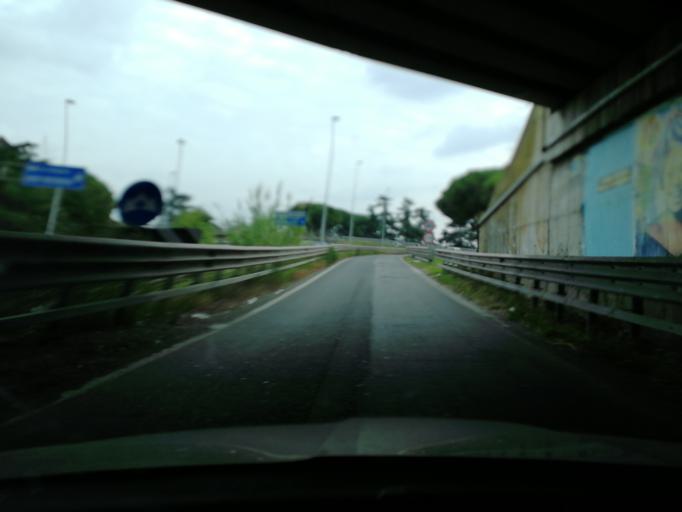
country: IT
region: Latium
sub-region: Citta metropolitana di Roma Capitale
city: Ciampino
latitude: 41.8376
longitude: 12.5903
